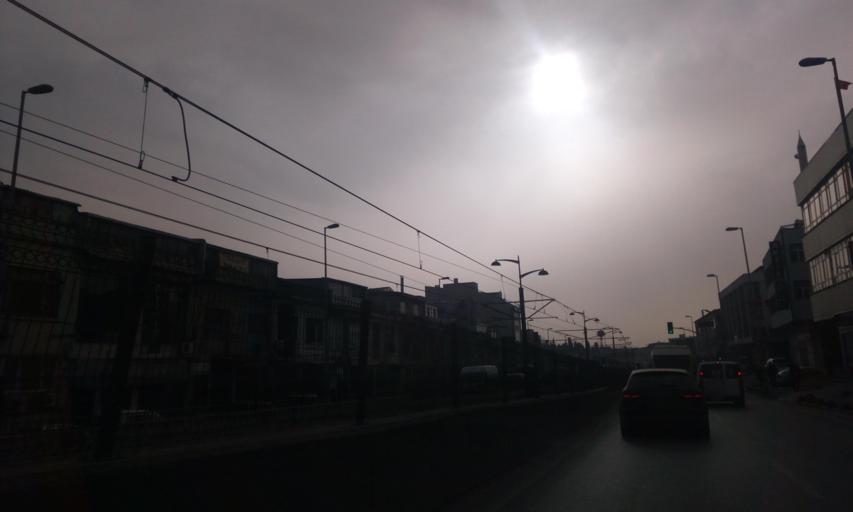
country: TR
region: Istanbul
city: Istanbul
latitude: 41.0381
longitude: 28.9227
